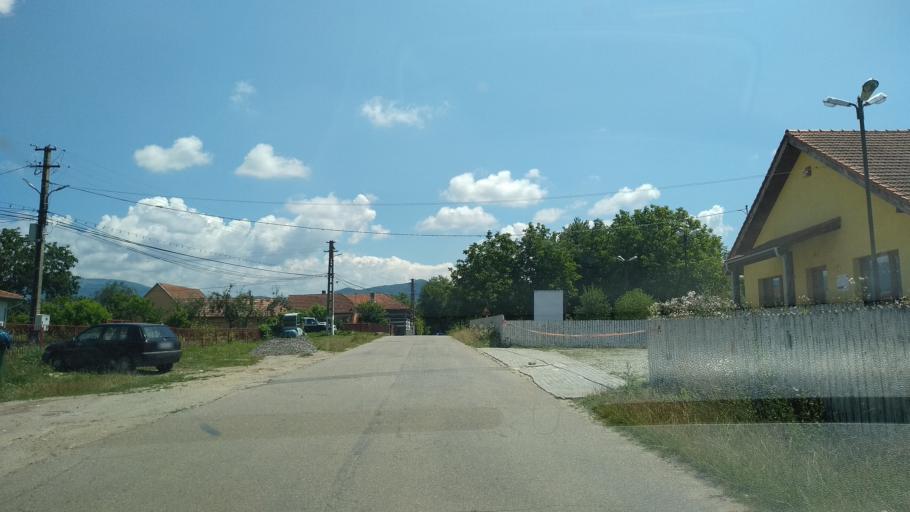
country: RO
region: Hunedoara
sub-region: Comuna Bosorod
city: Bosorod
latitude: 45.7047
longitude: 23.0664
